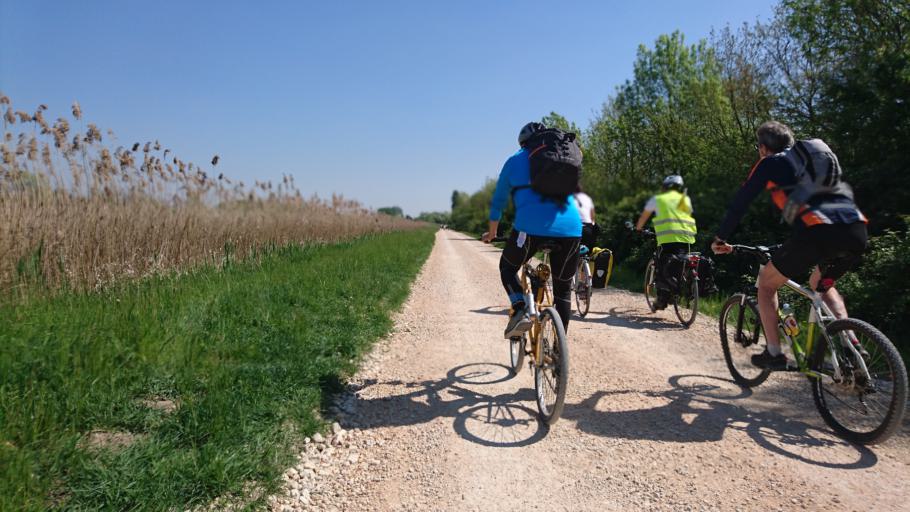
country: IT
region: Veneto
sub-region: Provincia di Venezia
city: Musile di Piave
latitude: 45.5767
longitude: 12.5432
